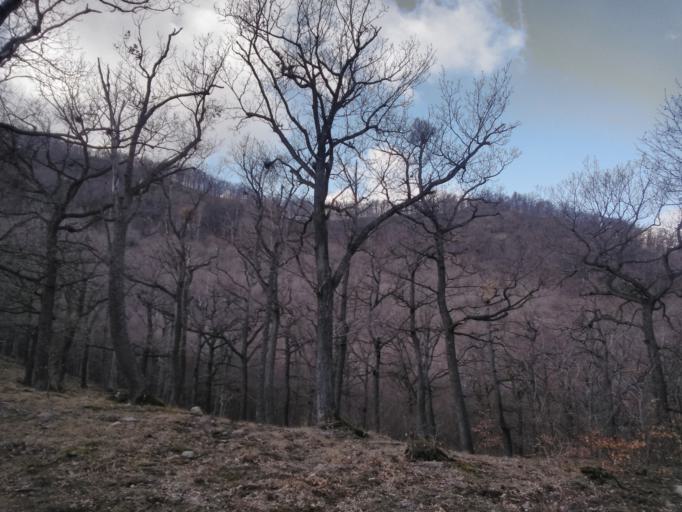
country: HU
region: Pest
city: Dunabogdany
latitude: 47.7509
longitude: 19.0418
